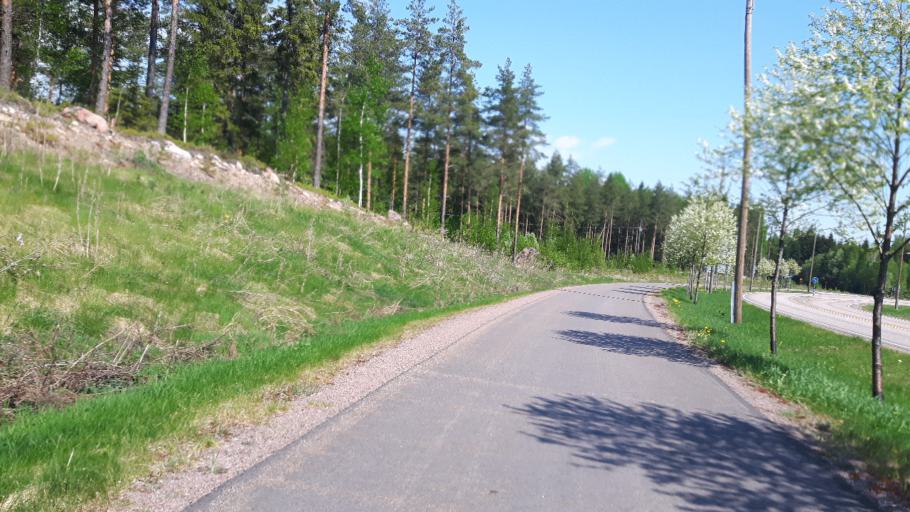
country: FI
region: Uusimaa
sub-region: Loviisa
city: Ruotsinpyhtaeae
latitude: 60.4943
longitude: 26.4206
